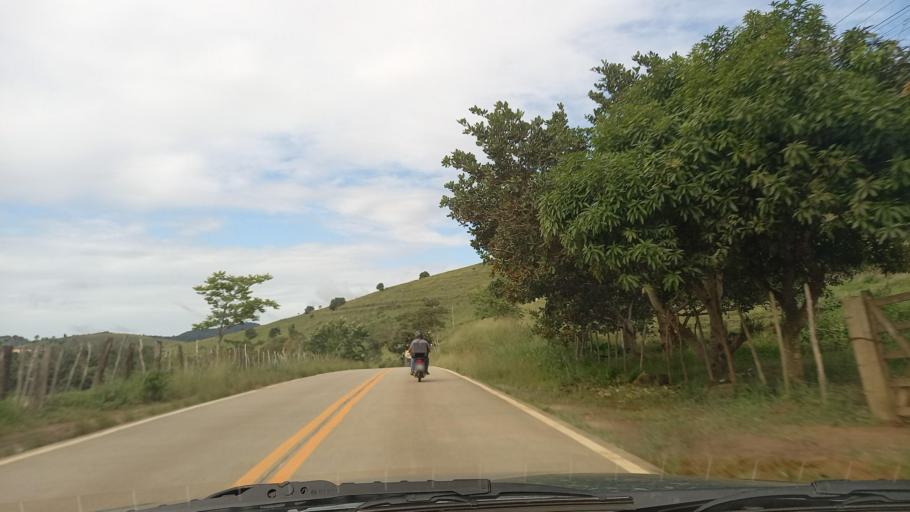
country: BR
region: Pernambuco
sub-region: Maraial
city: Maraial
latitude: -8.7503
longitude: -35.8224
